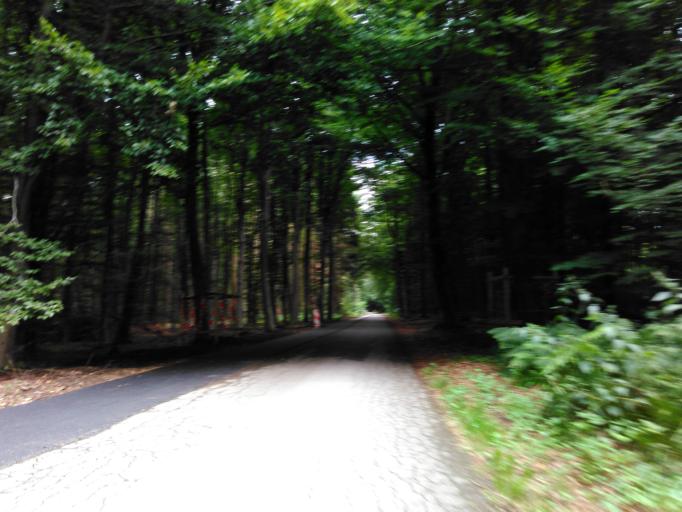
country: LU
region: Luxembourg
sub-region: Canton de Luxembourg
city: Sandweiler
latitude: 49.6442
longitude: 6.2116
